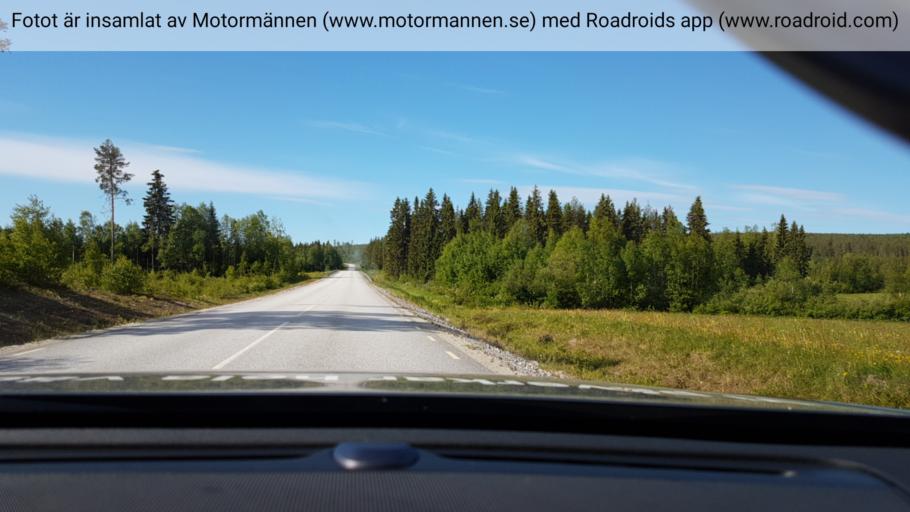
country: SE
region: Vaesterbotten
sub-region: Vindelns Kommun
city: Vindeln
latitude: 64.1954
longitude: 19.4122
